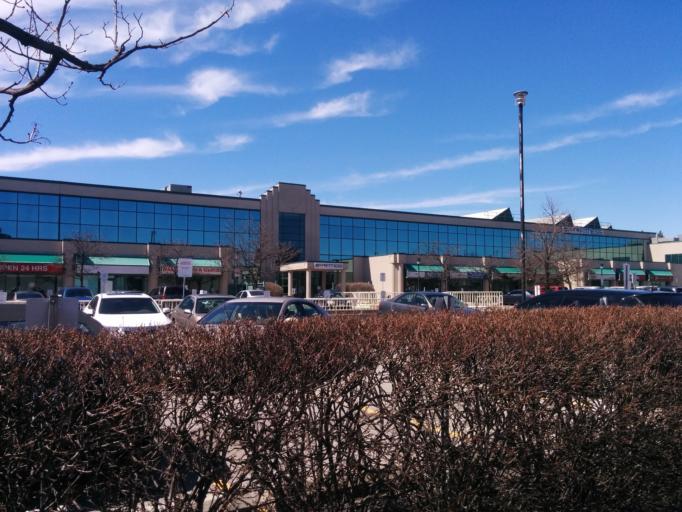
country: CA
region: Ontario
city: Toronto
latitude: 43.7135
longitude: -79.3595
